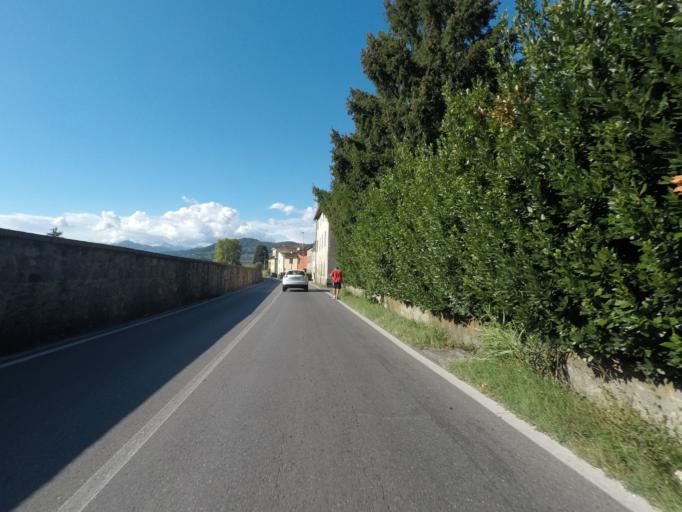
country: IT
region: Tuscany
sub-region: Provincia di Lucca
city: Lucca
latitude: 43.8670
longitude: 10.5084
